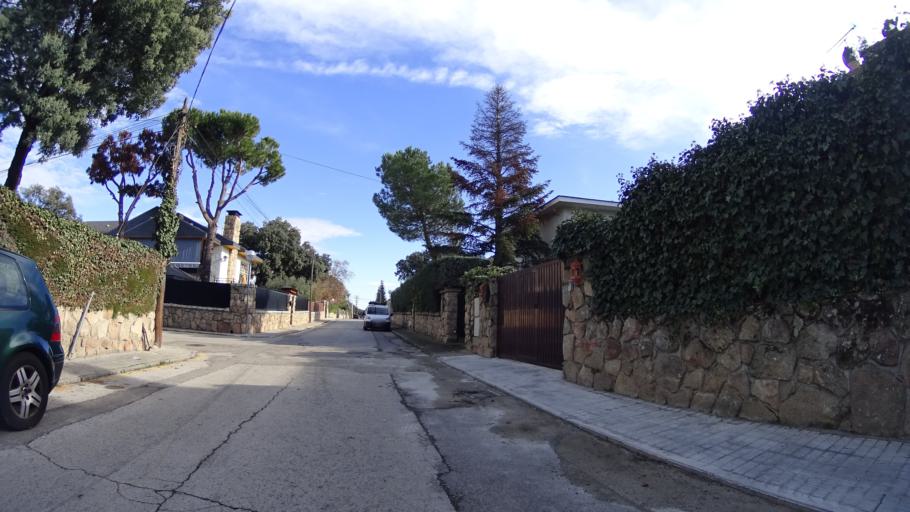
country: ES
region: Madrid
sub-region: Provincia de Madrid
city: Galapagar
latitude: 40.5818
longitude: -4.0201
